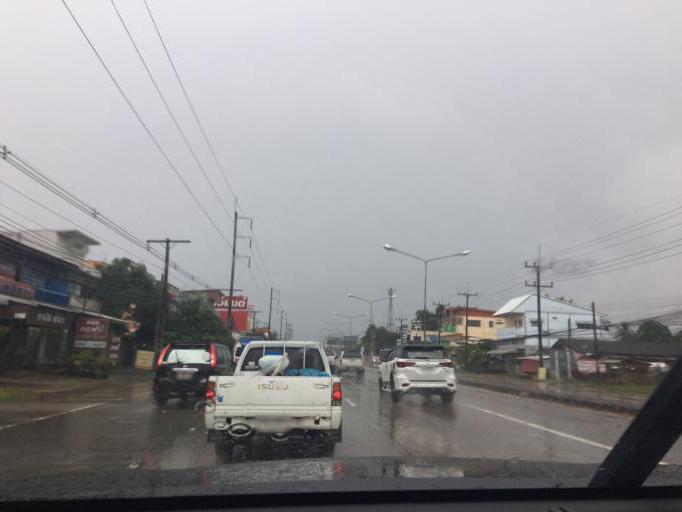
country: TH
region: Chiang Rai
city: Mae Fa Luang
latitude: 20.2655
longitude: 99.8584
